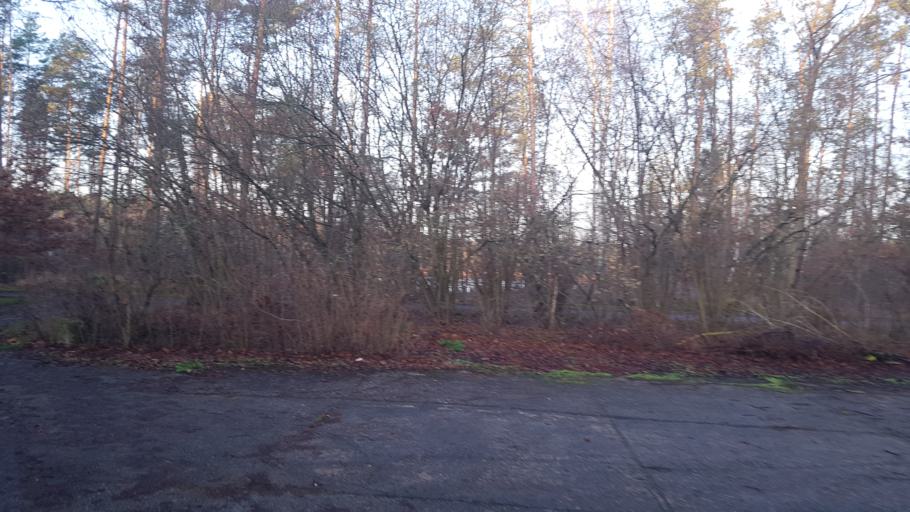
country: DE
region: Brandenburg
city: Ruckersdorf
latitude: 51.5896
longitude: 13.5881
